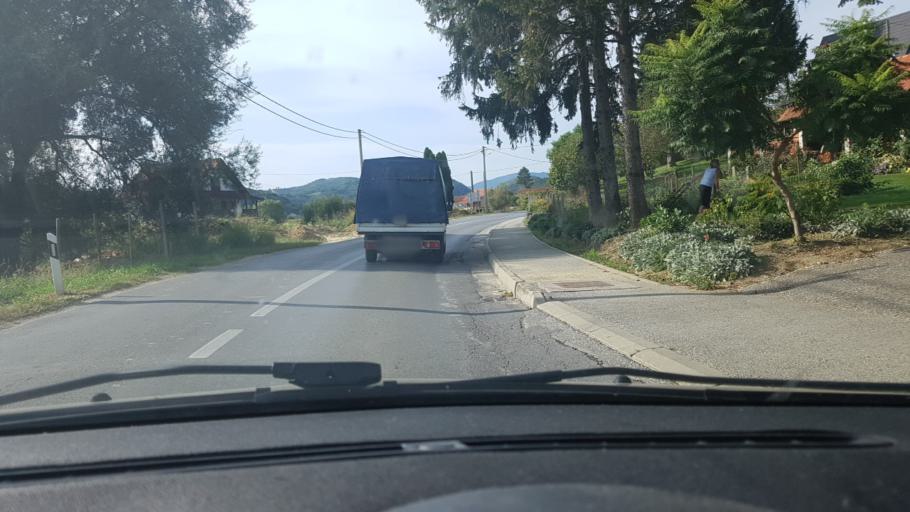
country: HR
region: Krapinsko-Zagorska
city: Zlatar
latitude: 46.0940
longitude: 16.0407
